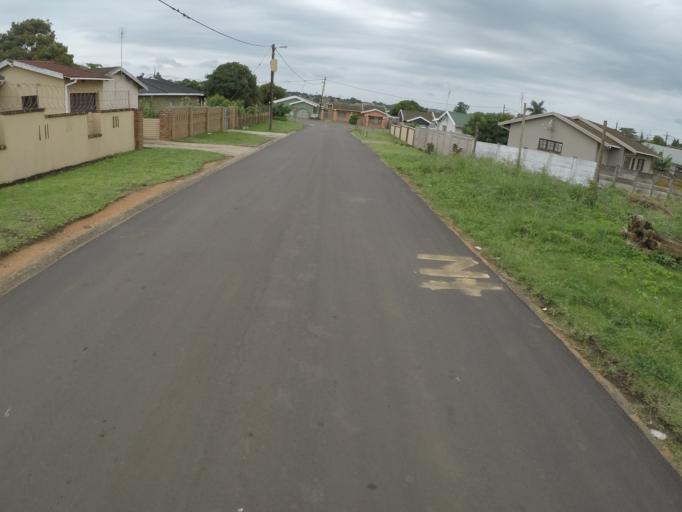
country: ZA
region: KwaZulu-Natal
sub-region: uThungulu District Municipality
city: Empangeni
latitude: -28.7744
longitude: 31.8506
